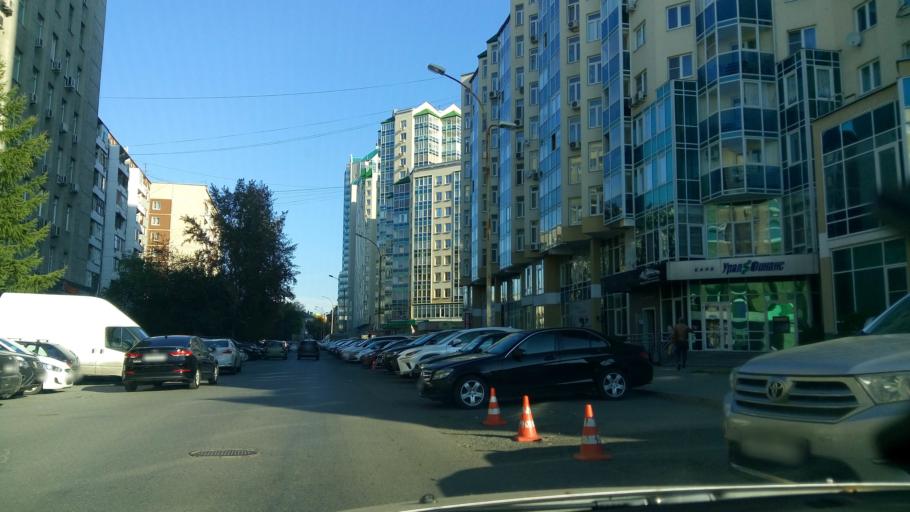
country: RU
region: Sverdlovsk
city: Yekaterinburg
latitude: 56.8459
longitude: 60.6212
